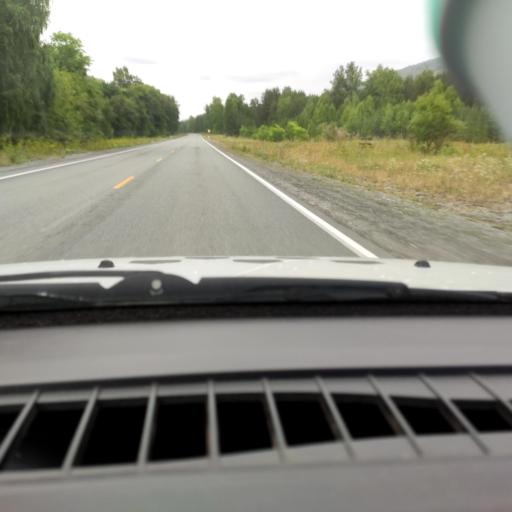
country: RU
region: Chelyabinsk
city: Turgoyak
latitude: 55.2992
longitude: 60.1988
